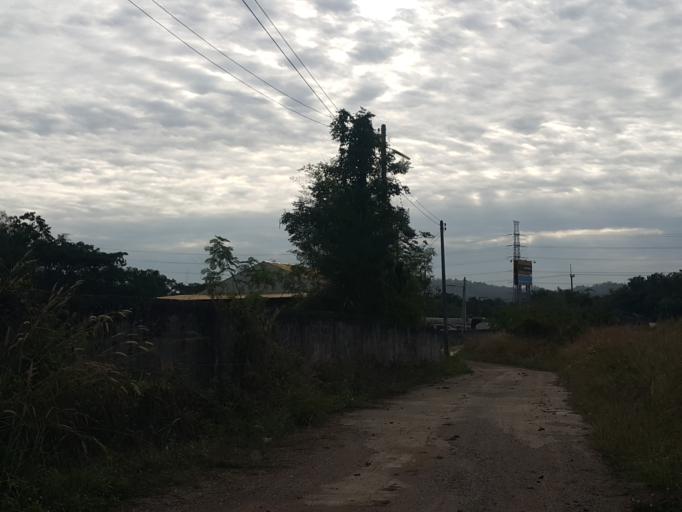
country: TH
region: Lampang
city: Mae Mo
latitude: 18.2472
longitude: 99.5953
